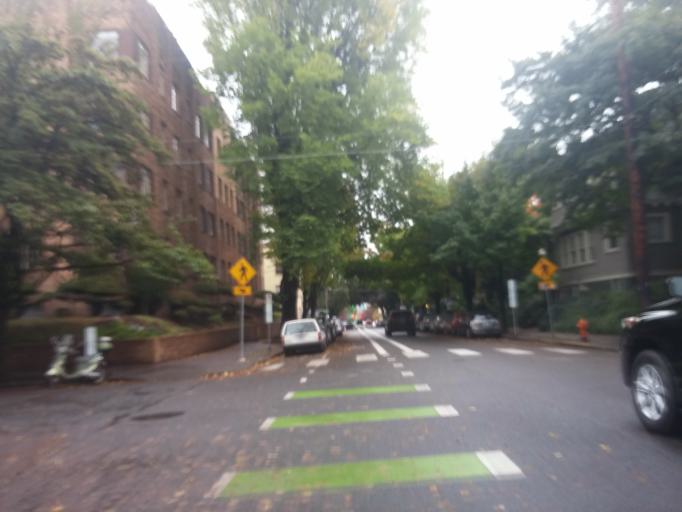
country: US
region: Oregon
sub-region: Multnomah County
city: Portland
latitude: 45.5250
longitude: -122.6929
